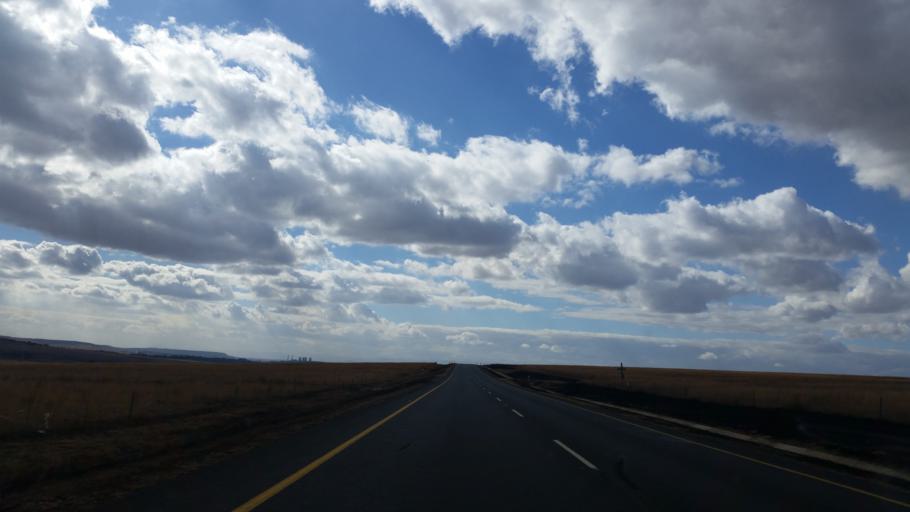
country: ZA
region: KwaZulu-Natal
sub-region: Amajuba District Municipality
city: Dannhauser
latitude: -27.9512
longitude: 29.9720
